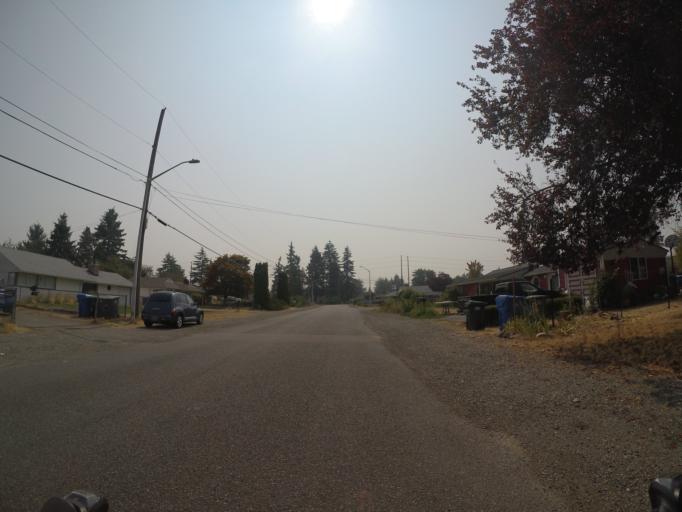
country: US
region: Washington
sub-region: Pierce County
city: Lakewood
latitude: 47.1579
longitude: -122.5105
